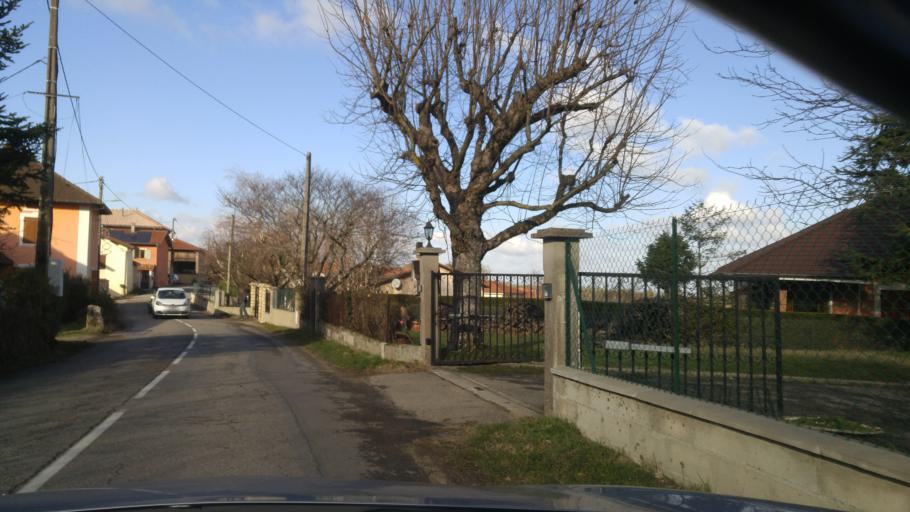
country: FR
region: Rhone-Alpes
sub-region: Departement de l'Isere
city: Roche
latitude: 45.5846
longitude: 5.1654
